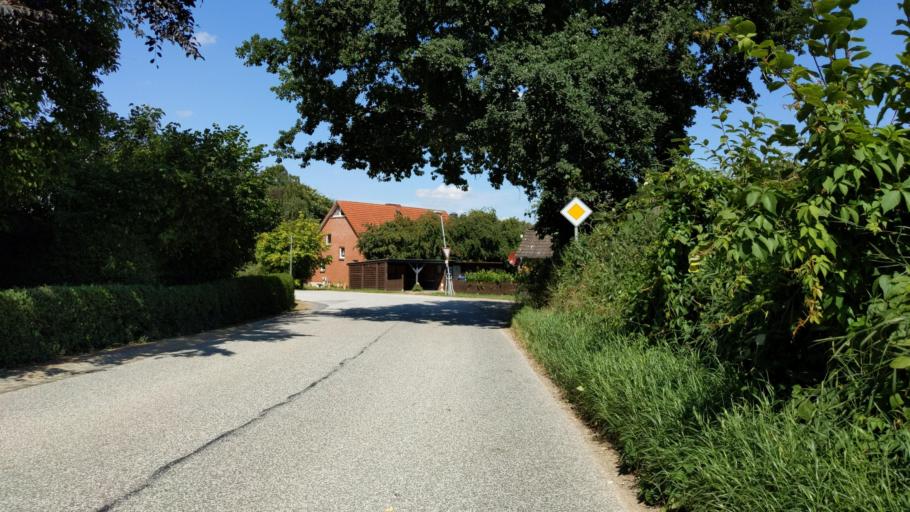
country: DE
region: Schleswig-Holstein
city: Krummesse
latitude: 53.8152
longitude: 10.6766
